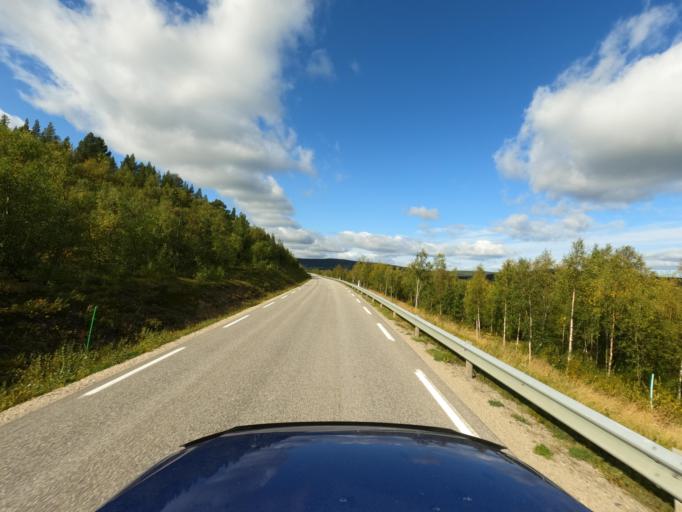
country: NO
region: Finnmark Fylke
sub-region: Karasjok
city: Karasjohka
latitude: 69.4547
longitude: 25.5707
